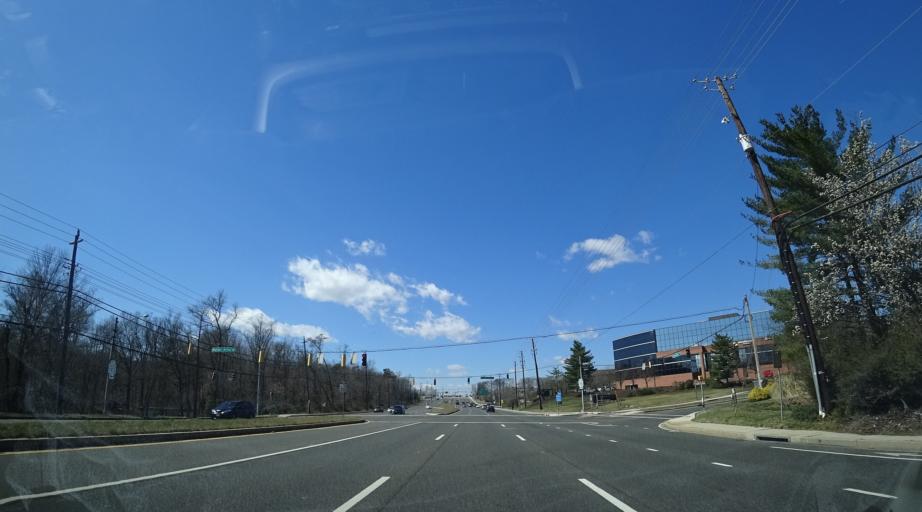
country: US
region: Maryland
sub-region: Prince George's County
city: Berwyn Heights
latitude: 38.9962
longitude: -76.8945
